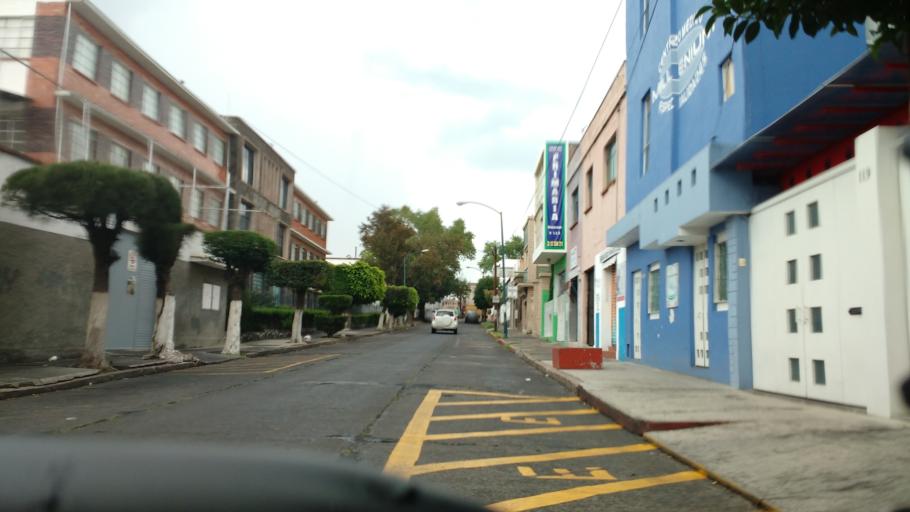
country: MX
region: Michoacan
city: Morelia
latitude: 19.7009
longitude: -101.1838
